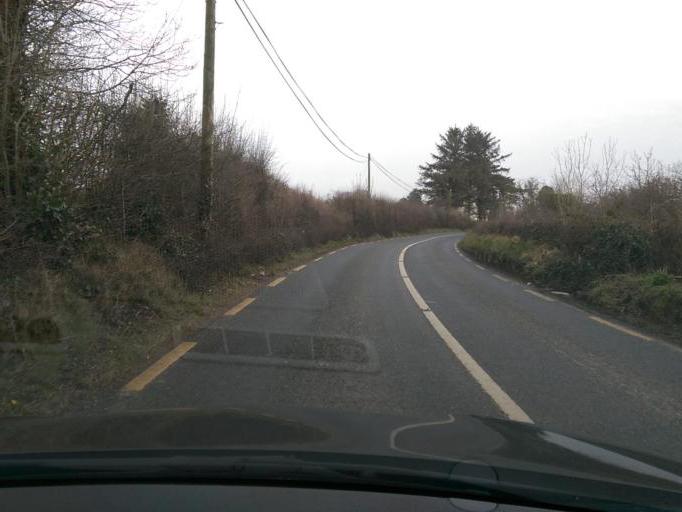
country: IE
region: Connaught
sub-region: Roscommon
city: Roscommon
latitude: 53.5121
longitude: -8.4129
